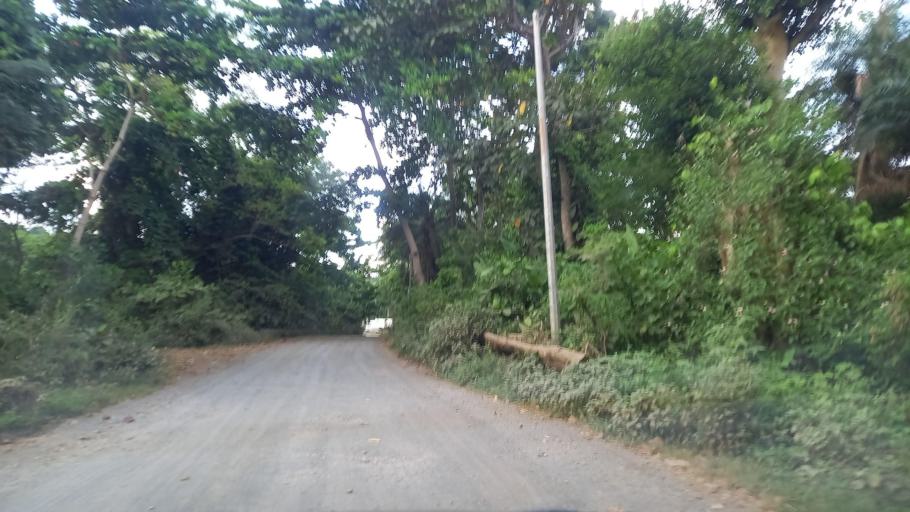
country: YT
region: Dembeni
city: Dembeni
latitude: -12.8293
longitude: 45.1916
